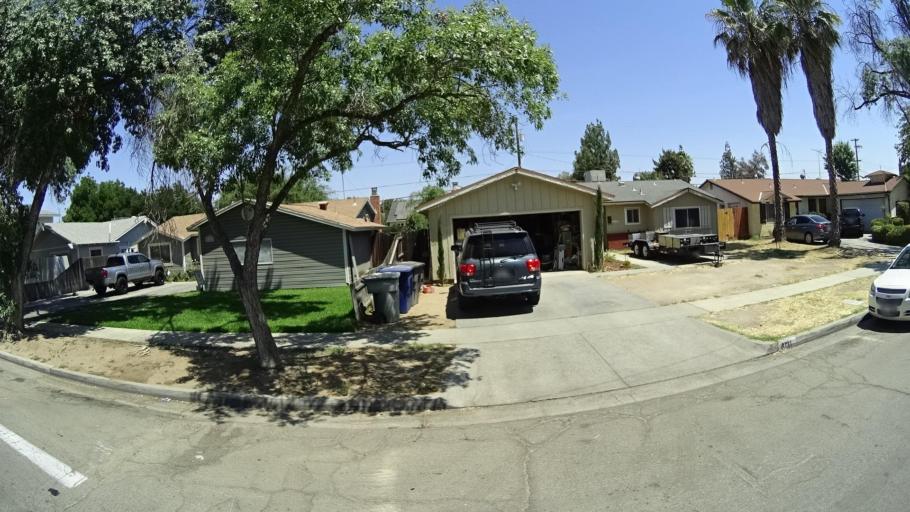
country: US
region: California
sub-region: Fresno County
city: Fresno
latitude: 36.7973
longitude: -119.7560
